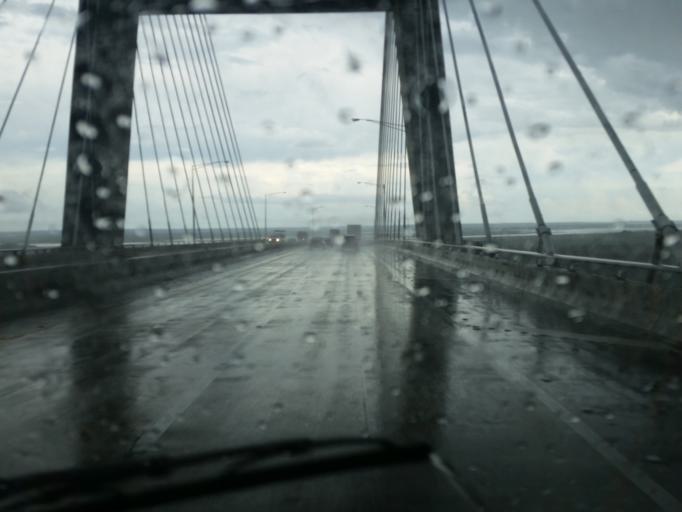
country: US
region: Alabama
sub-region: Mobile County
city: Prichard
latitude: 30.7333
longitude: -88.0423
